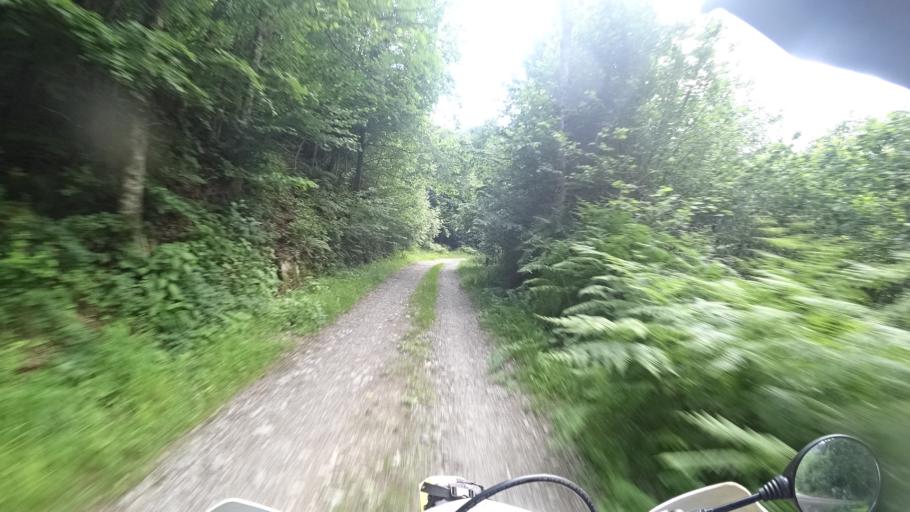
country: SI
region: Osilnica
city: Osilnica
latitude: 45.4644
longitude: 14.7125
